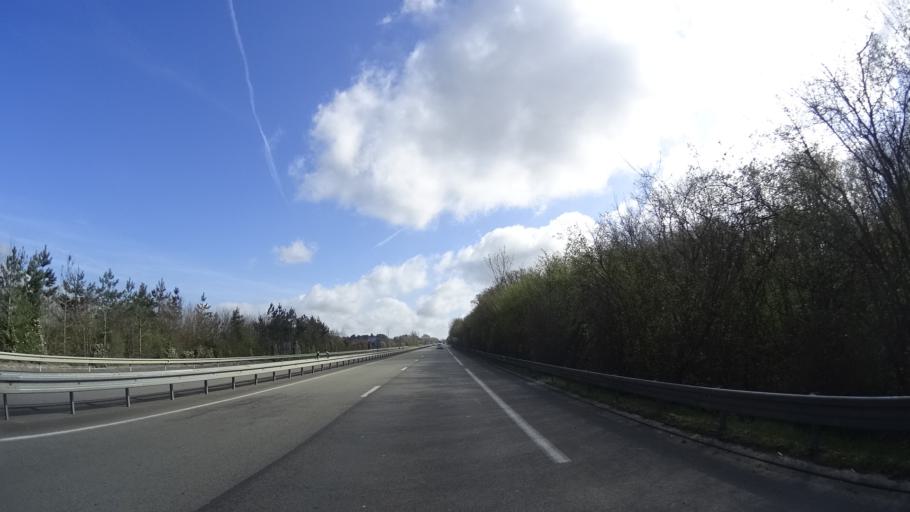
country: FR
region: Pays de la Loire
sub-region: Departement de Maine-et-Loire
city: Segre
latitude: 47.6946
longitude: -0.8870
